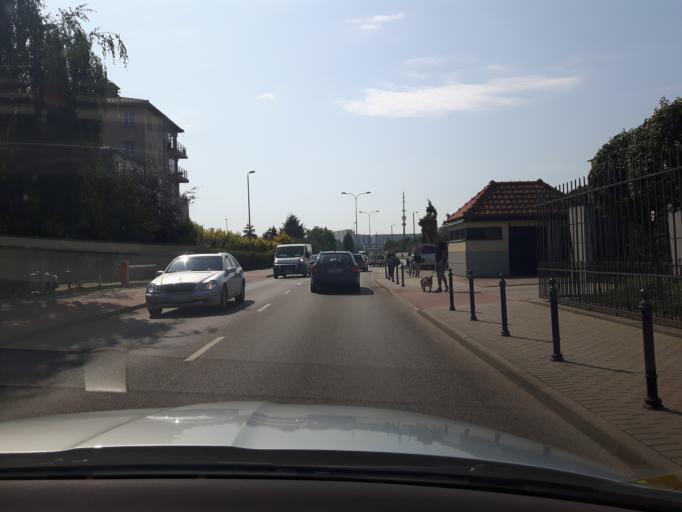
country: PL
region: Pomeranian Voivodeship
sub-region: Sopot
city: Sopot
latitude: 54.4299
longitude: 18.5740
